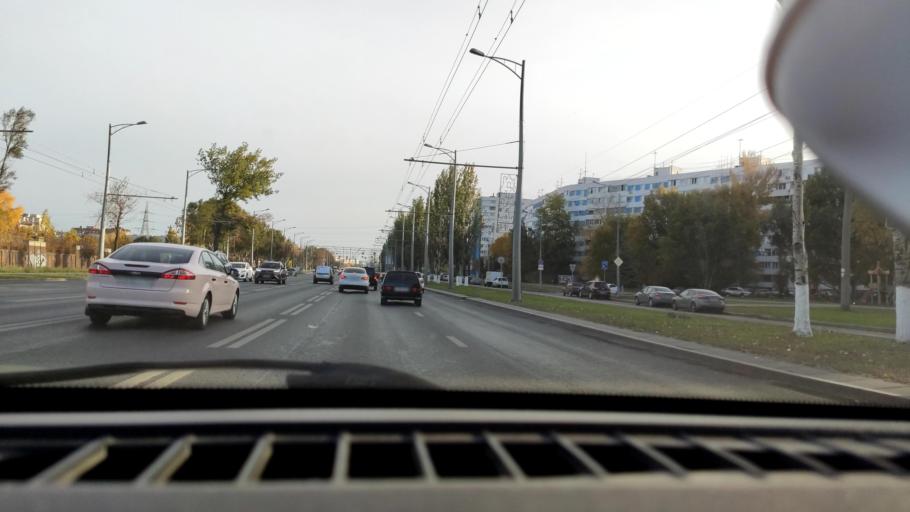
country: RU
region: Samara
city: Samara
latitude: 53.2378
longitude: 50.2035
